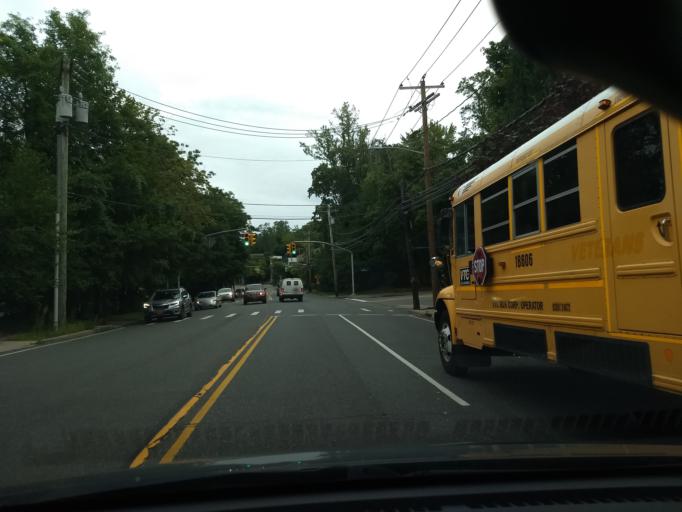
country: US
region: New York
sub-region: Nassau County
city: Thomaston
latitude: 40.7942
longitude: -73.7126
